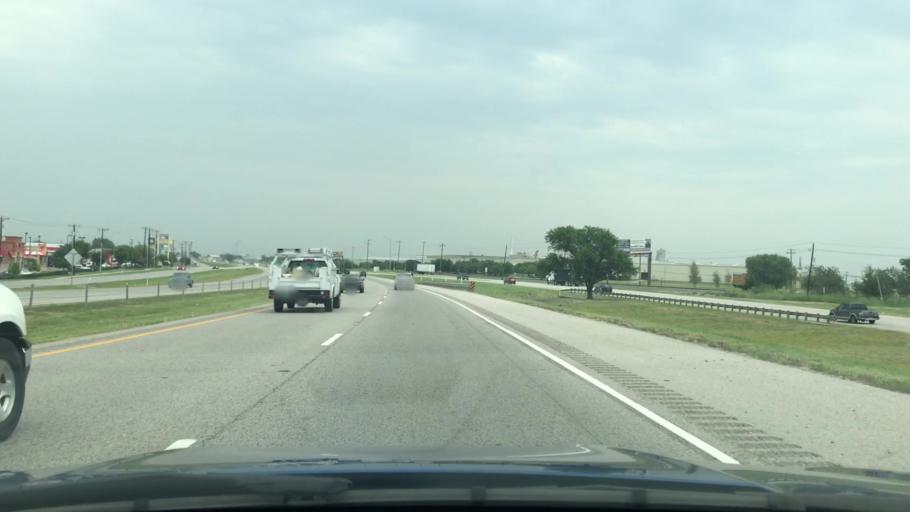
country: US
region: Texas
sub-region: Kaufman County
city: Forney
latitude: 32.7420
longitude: -96.4467
